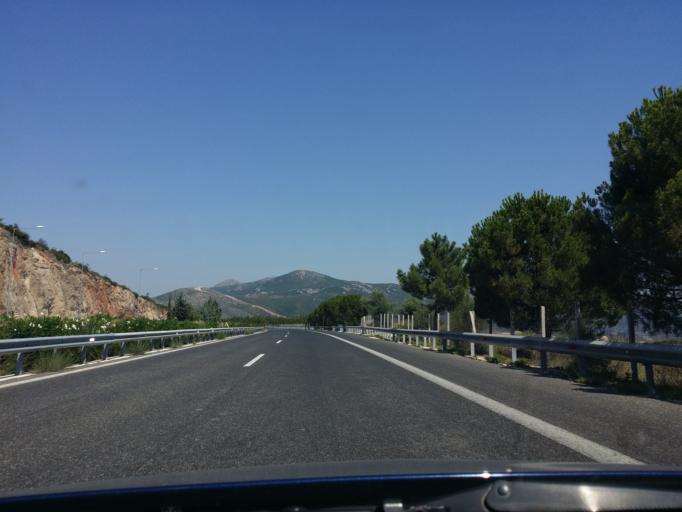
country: GR
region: Peloponnese
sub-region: Nomos Korinthias
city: Nemea
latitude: 37.7832
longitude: 22.6955
